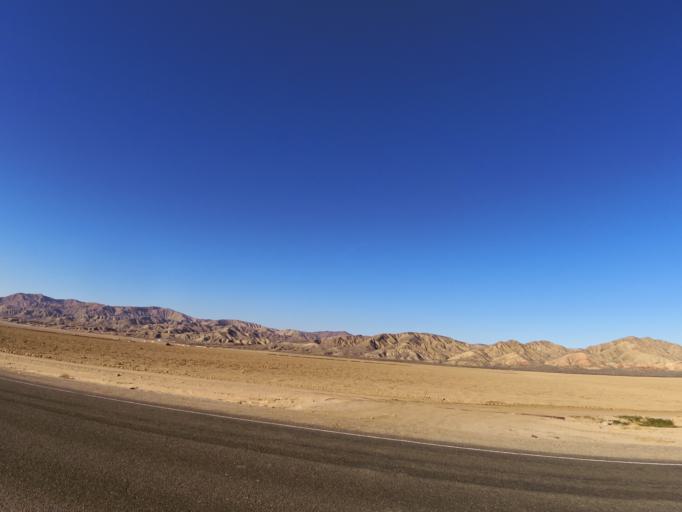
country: US
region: California
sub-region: Kern County
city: Maricopa
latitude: 34.9361
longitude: -119.5133
